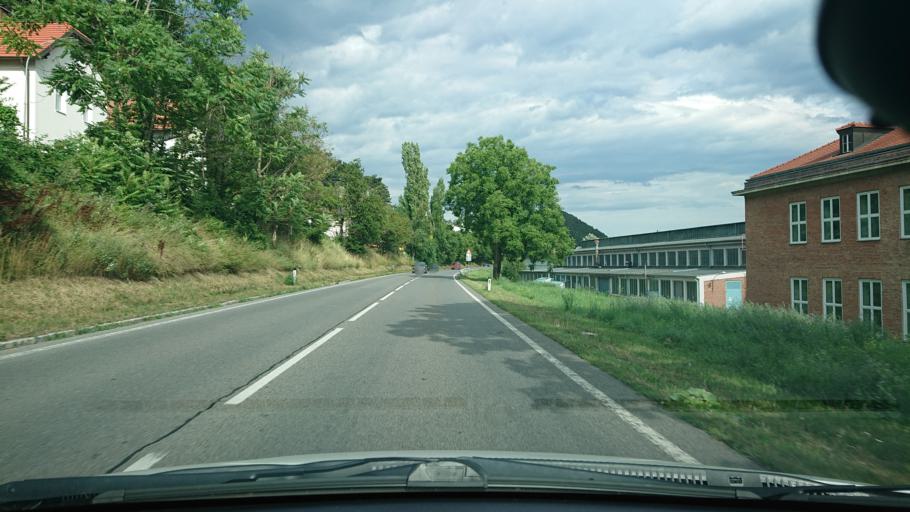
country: AT
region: Lower Austria
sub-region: Politischer Bezirk Baden
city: Berndorf
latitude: 47.9446
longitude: 16.1276
